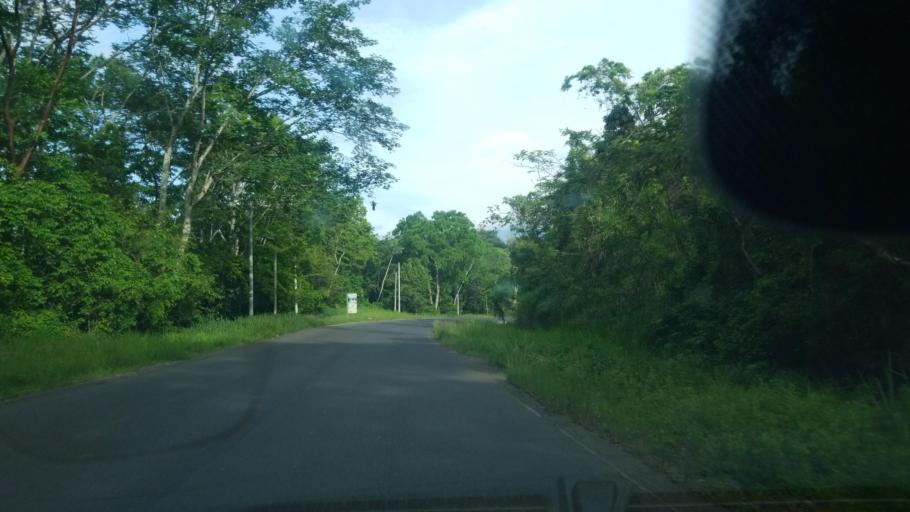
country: HN
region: Santa Barbara
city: Trinidad
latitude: 15.1803
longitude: -88.2728
